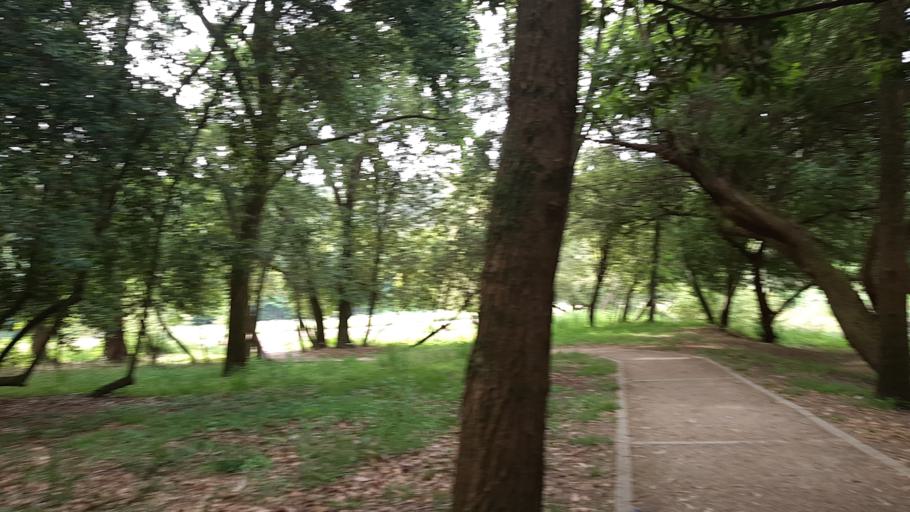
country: ES
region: Galicia
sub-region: Provincia de Pontevedra
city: O Rosal
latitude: 41.9209
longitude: -8.8271
